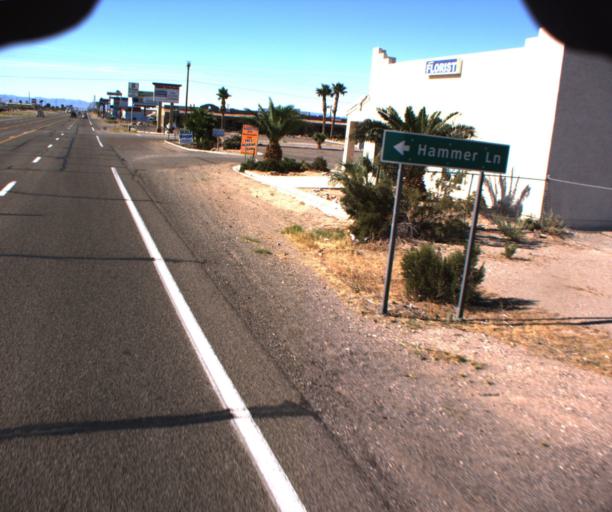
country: US
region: Arizona
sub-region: Mohave County
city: Mohave Valley
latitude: 35.0052
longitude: -114.5981
